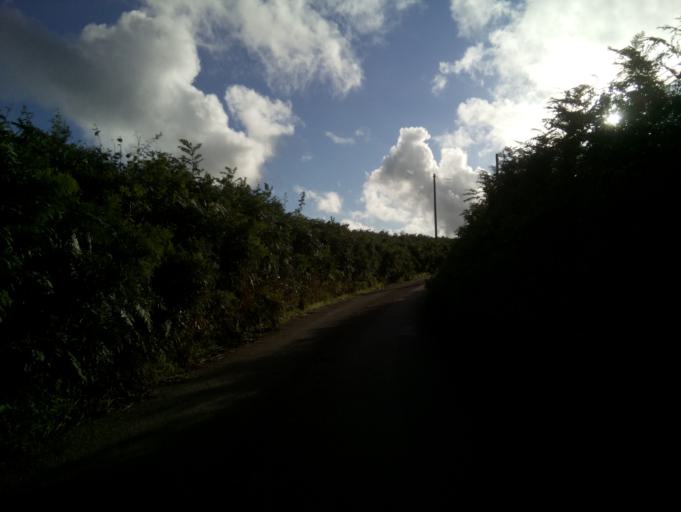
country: GB
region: England
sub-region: Devon
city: Dartmouth
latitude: 50.3457
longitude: -3.6515
